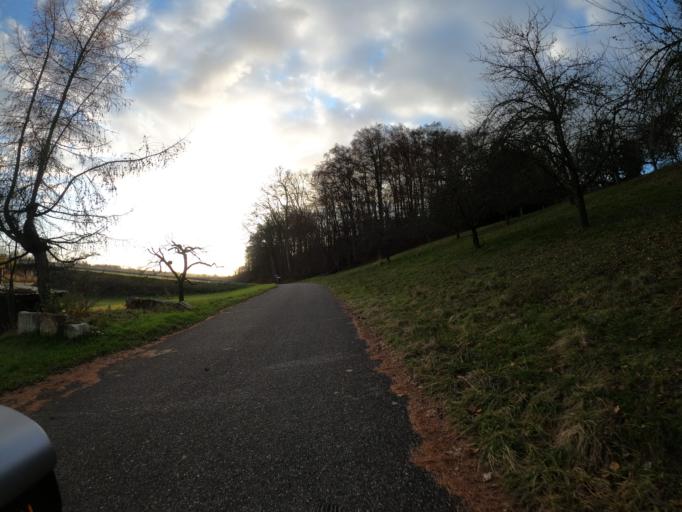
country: DE
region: Baden-Wuerttemberg
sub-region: Regierungsbezirk Stuttgart
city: Wernau
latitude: 48.7006
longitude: 9.4096
